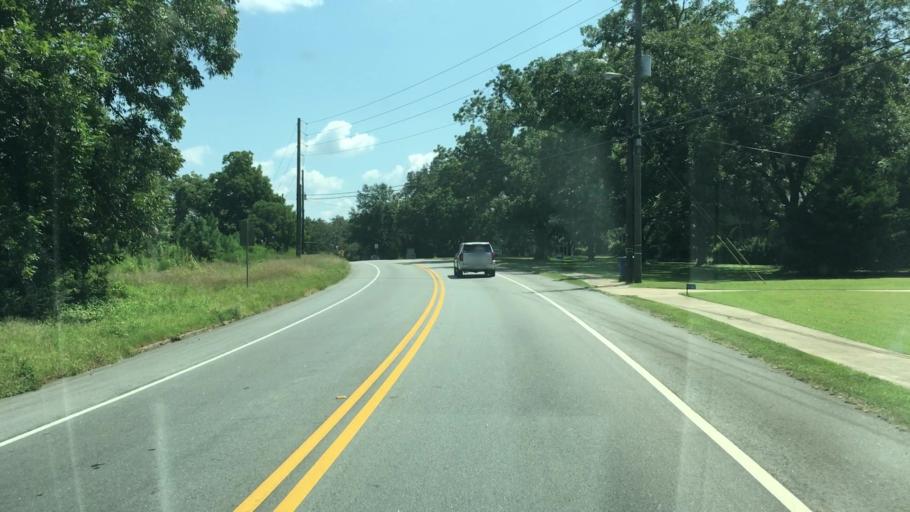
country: US
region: Georgia
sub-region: Oconee County
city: Watkinsville
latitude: 33.8229
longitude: -83.4407
